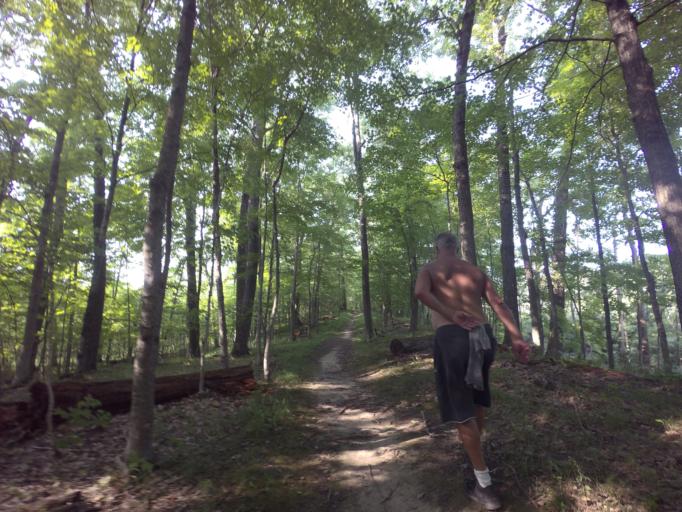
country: US
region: Wisconsin
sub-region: Washington County
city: Kewaskum
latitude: 43.5889
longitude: -88.1778
